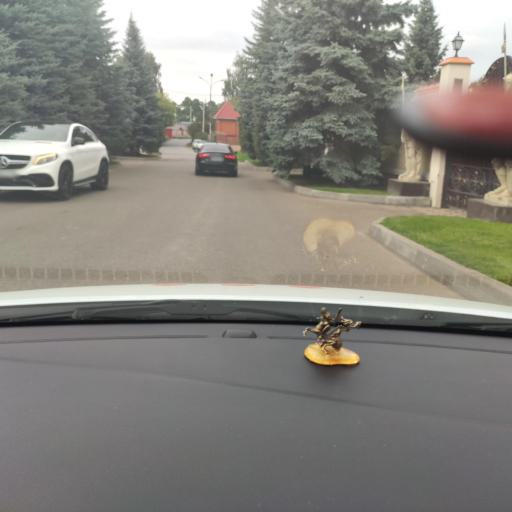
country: RU
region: Tatarstan
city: Verkhniy Uslon
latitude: 55.6176
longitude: 49.0156
